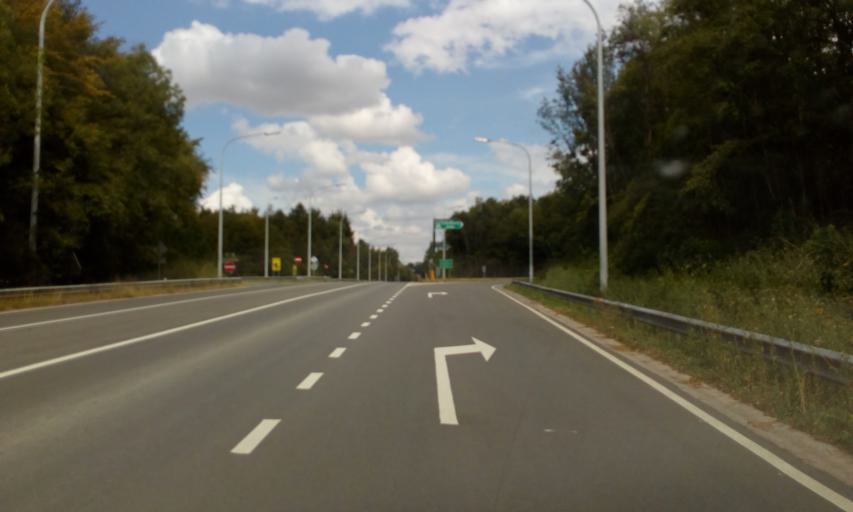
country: BE
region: Wallonia
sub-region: Province de Namur
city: Assesse
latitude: 50.3285
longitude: 5.0159
